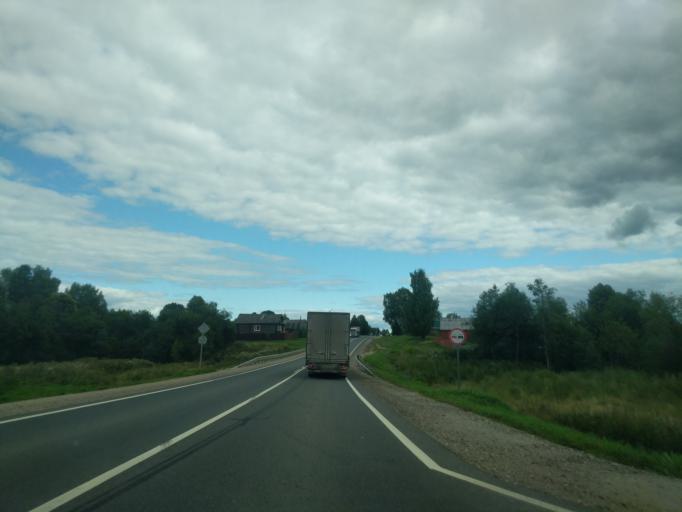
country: RU
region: Kostroma
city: Ostrovskoye
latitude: 57.8227
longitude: 42.1923
